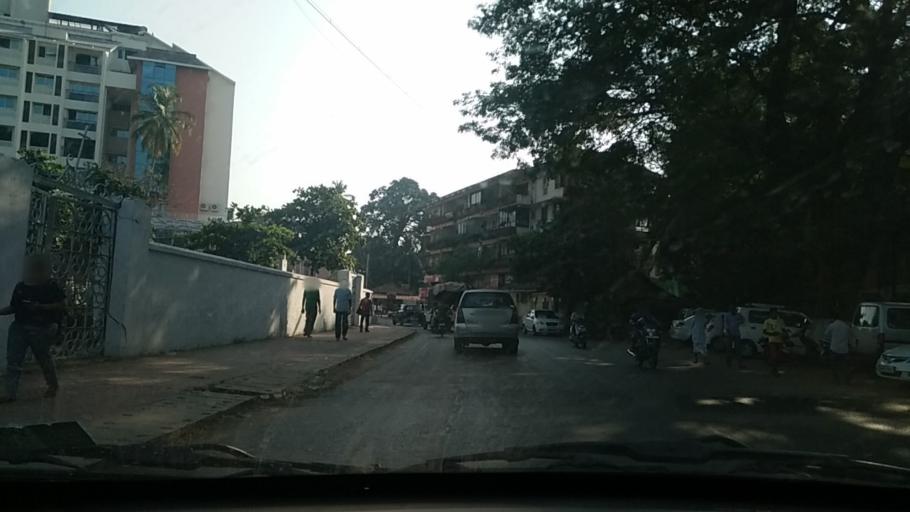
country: IN
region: Goa
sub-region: North Goa
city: Panaji
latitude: 15.4909
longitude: 73.8200
